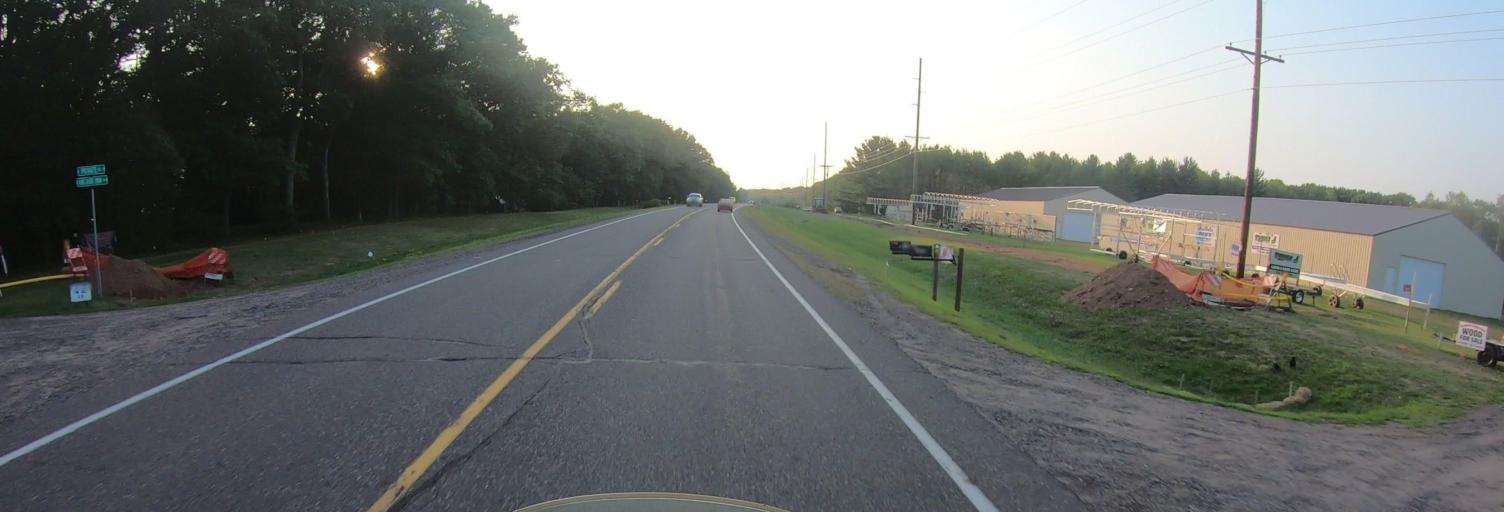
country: US
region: Wisconsin
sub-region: Burnett County
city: Siren
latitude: 45.8163
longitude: -92.2380
